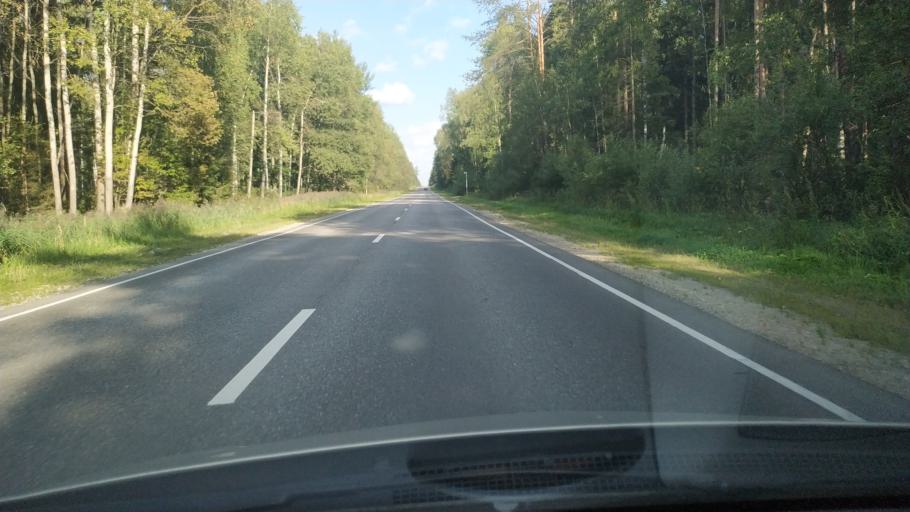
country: RU
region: Moskovskaya
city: Vereya
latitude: 55.7026
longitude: 39.1946
